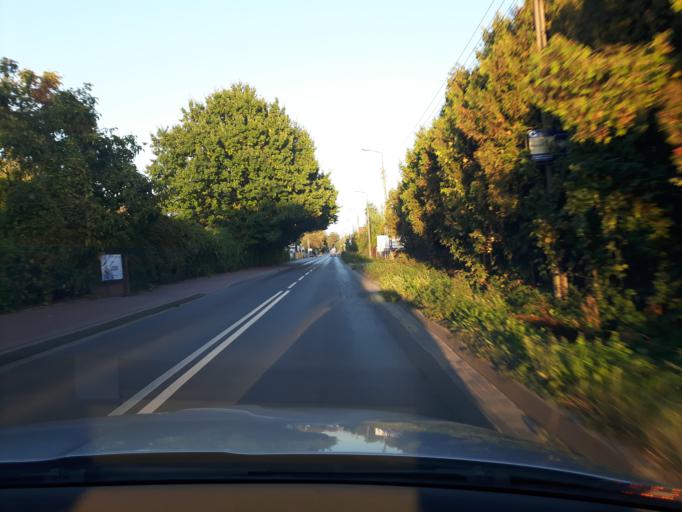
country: PL
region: Masovian Voivodeship
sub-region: Powiat wolominski
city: Kobylka
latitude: 52.3384
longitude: 21.1858
